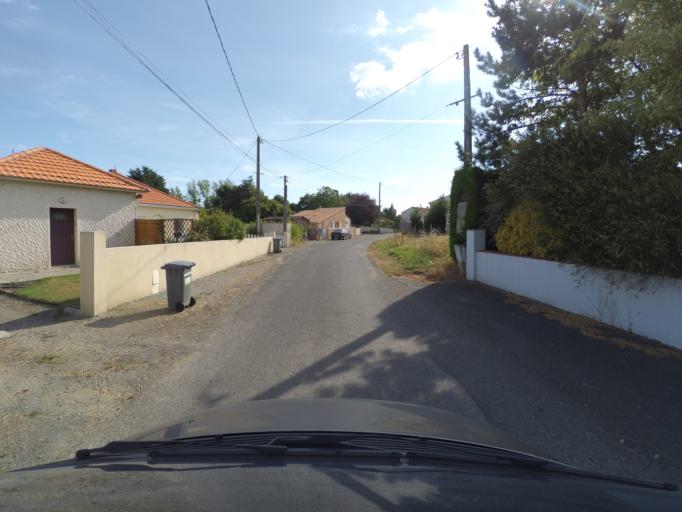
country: FR
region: Pays de la Loire
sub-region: Departement de la Loire-Atlantique
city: Montbert
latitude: 47.0514
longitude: -1.4850
